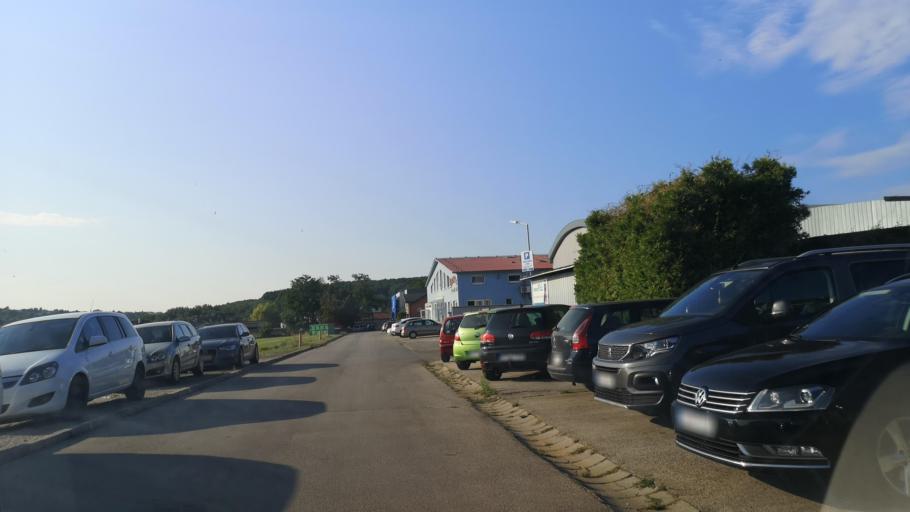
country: SK
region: Nitriansky
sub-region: Okres Nitra
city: Nitra
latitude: 48.3141
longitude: 18.0309
